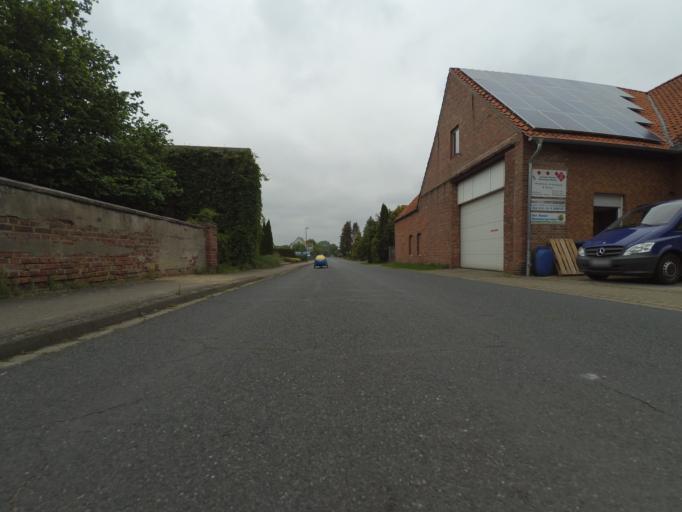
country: DE
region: Lower Saxony
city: Edemissen
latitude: 52.3987
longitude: 10.3223
